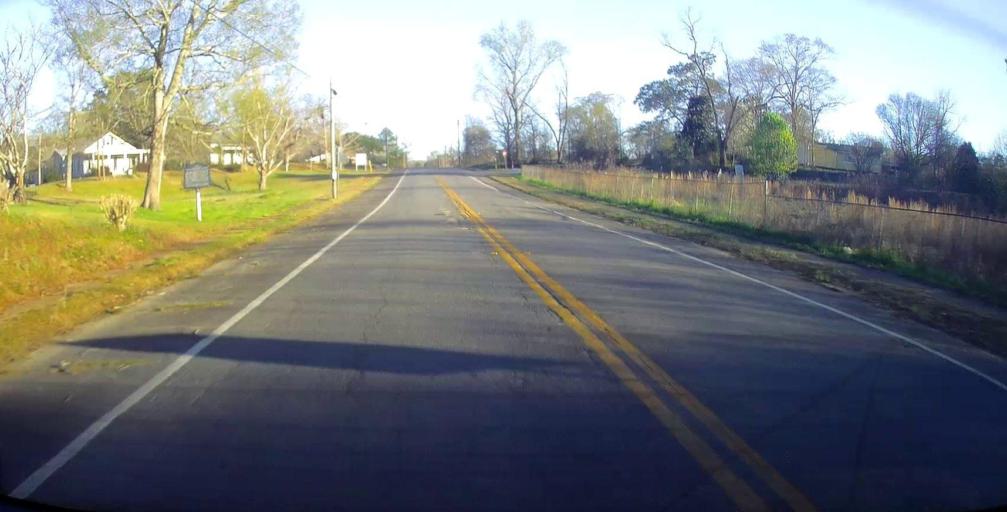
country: US
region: Georgia
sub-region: Talbot County
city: Talbotton
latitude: 32.6738
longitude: -84.5390
